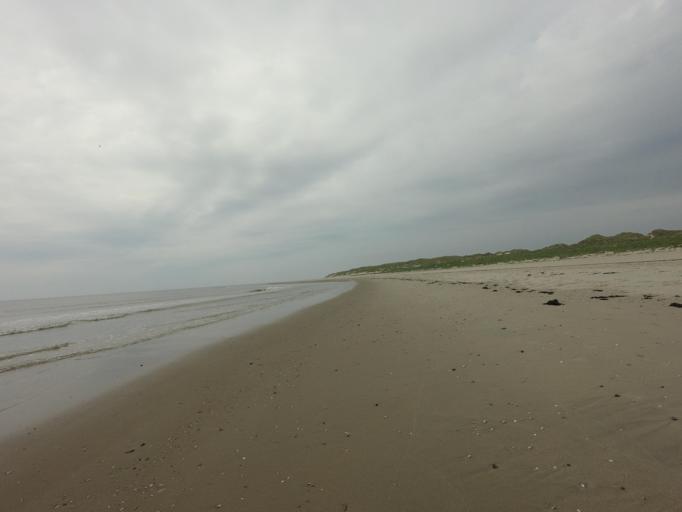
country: NL
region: North Holland
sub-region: Gemeente Den Helder
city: Den Helder
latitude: 53.0054
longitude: 4.7114
